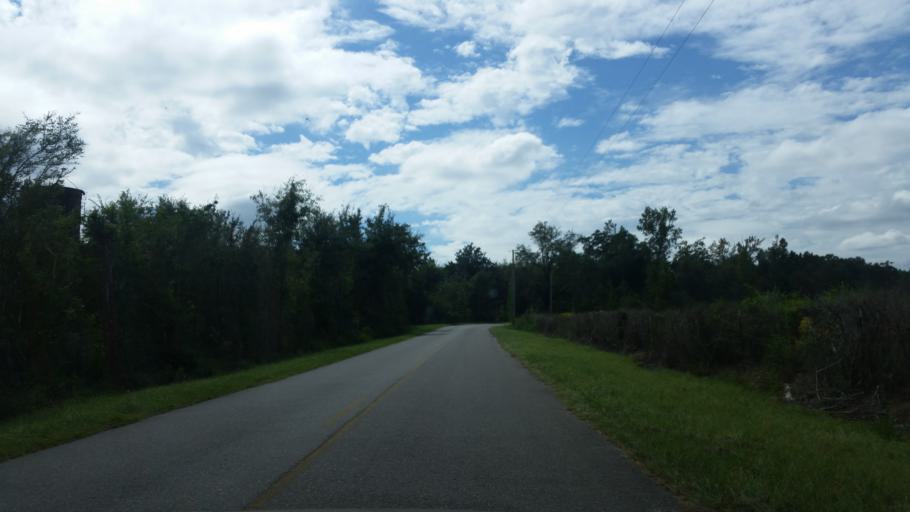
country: US
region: Florida
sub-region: Santa Rosa County
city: Point Baker
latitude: 30.7341
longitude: -87.0376
